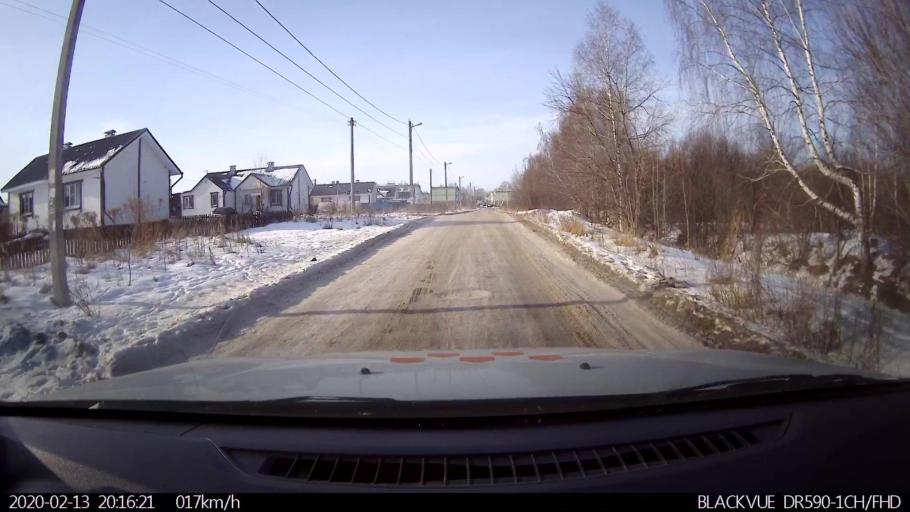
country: RU
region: Nizjnij Novgorod
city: Burevestnik
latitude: 56.2074
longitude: 43.8150
